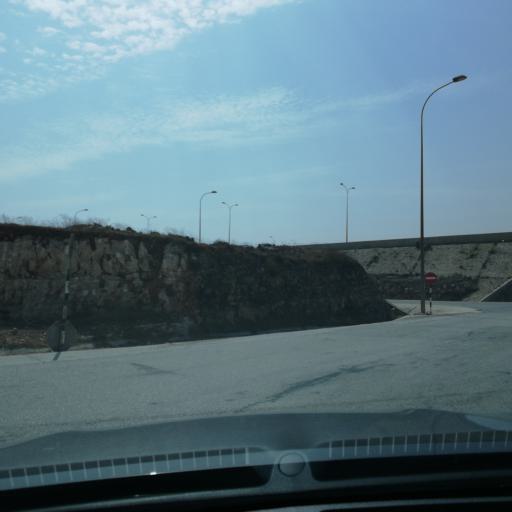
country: OM
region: Zufar
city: Salalah
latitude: 17.2452
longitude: 54.0737
